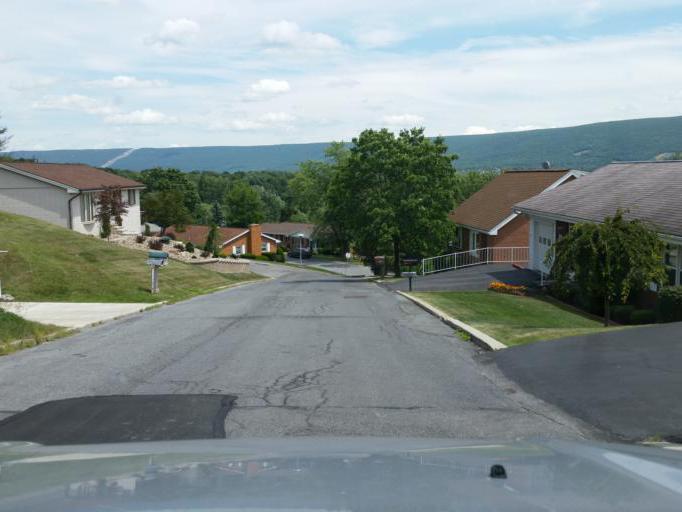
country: US
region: Pennsylvania
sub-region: Blair County
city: Altoona
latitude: 40.5359
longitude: -78.4071
